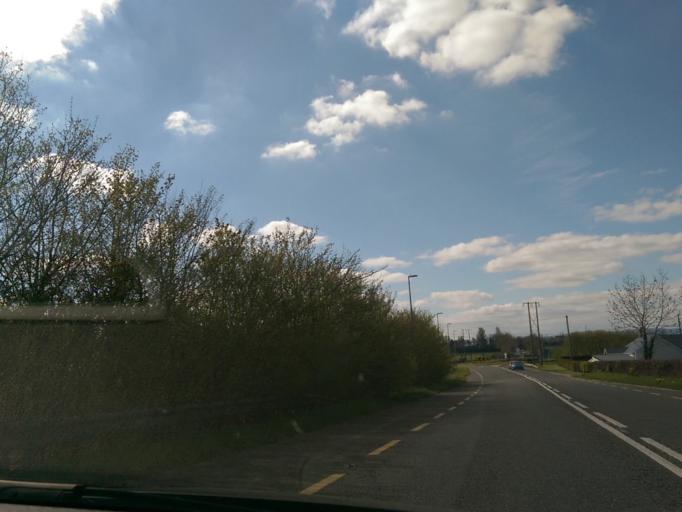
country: IE
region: Leinster
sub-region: Laois
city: Portlaoise
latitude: 53.0310
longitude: -7.2574
